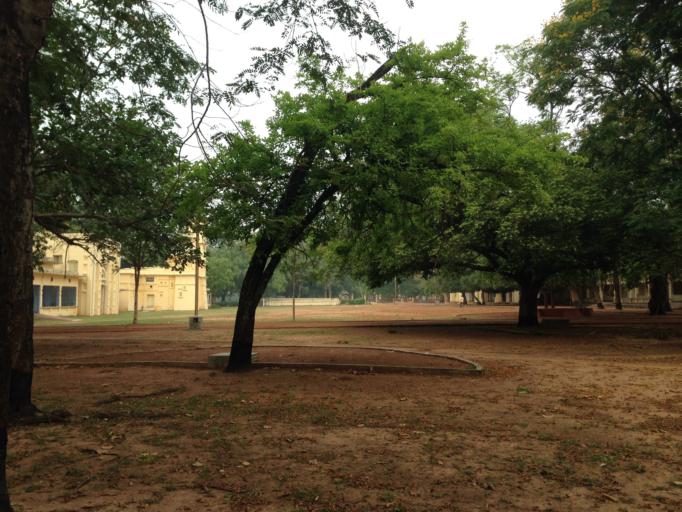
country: IN
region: West Bengal
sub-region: Birbhum
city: Bolpur
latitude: 23.6802
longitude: 87.6865
